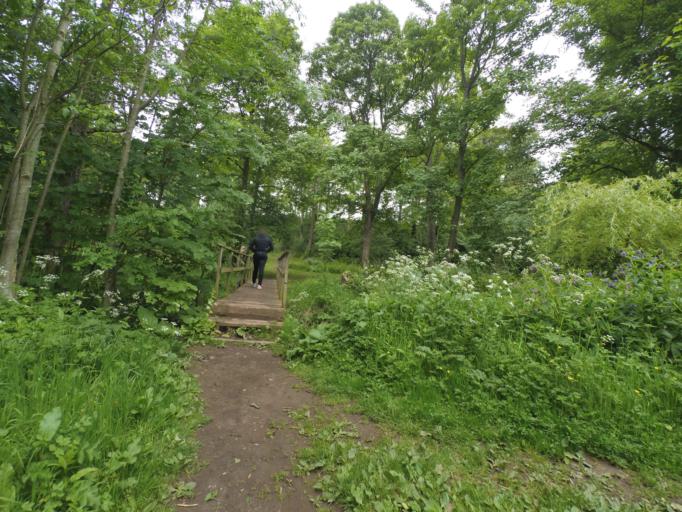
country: GB
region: Scotland
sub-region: East Lothian
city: Pencaitland
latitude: 55.9137
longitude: -2.8980
